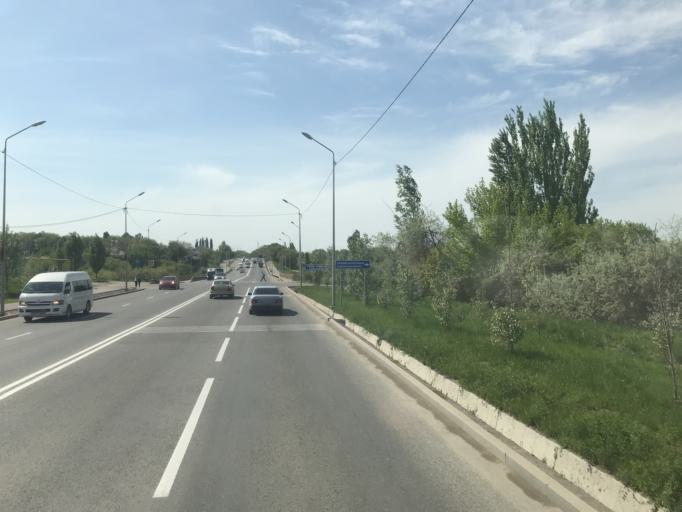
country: KZ
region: Almaty Oblysy
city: Burunday
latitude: 43.3098
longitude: 76.8707
